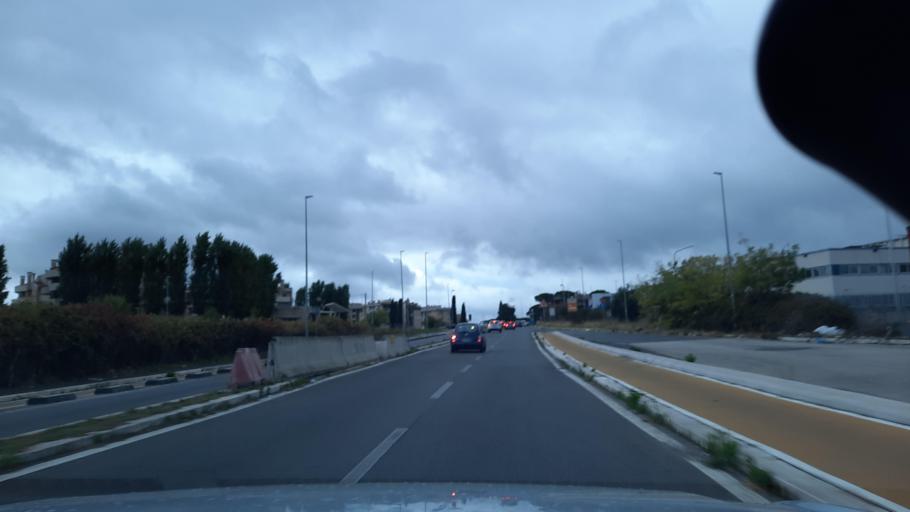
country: IT
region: Latium
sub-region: Citta metropolitana di Roma Capitale
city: Ciampino
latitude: 41.8465
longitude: 12.6124
